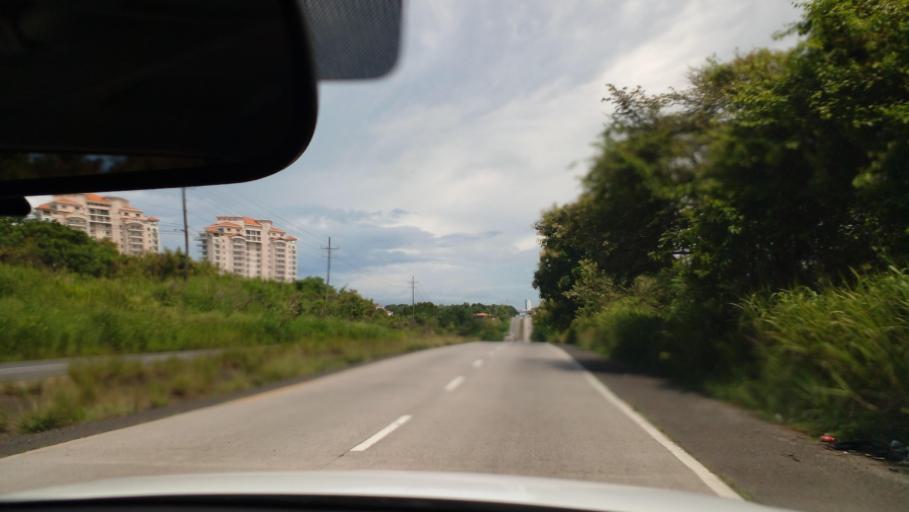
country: PA
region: Panama
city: Nueva Gorgona
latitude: 8.4972
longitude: -79.9583
